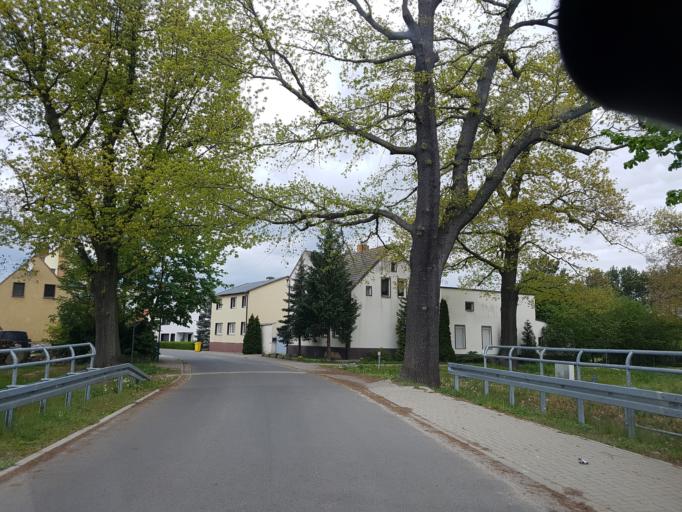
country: DE
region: Brandenburg
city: Altdobern
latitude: 51.6497
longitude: 14.0393
